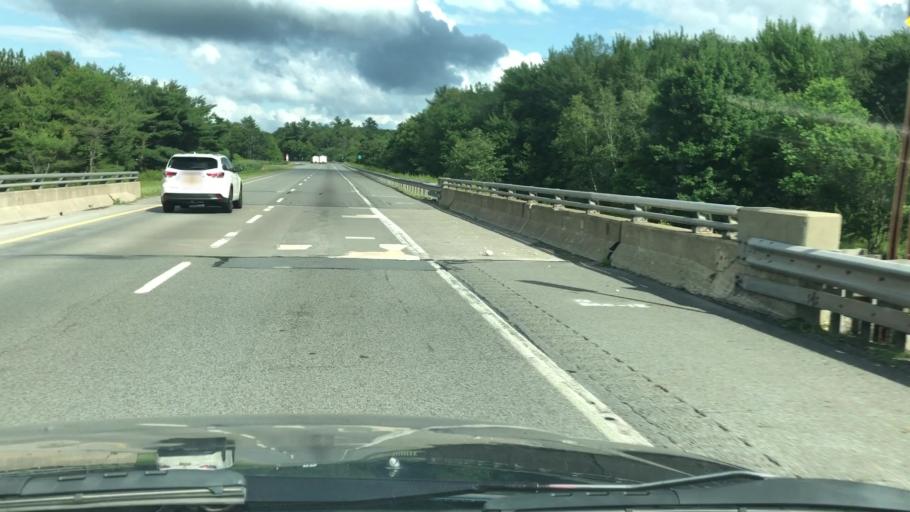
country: US
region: Pennsylvania
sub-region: Pike County
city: Gold Key Lake
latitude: 41.3436
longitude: -74.9224
